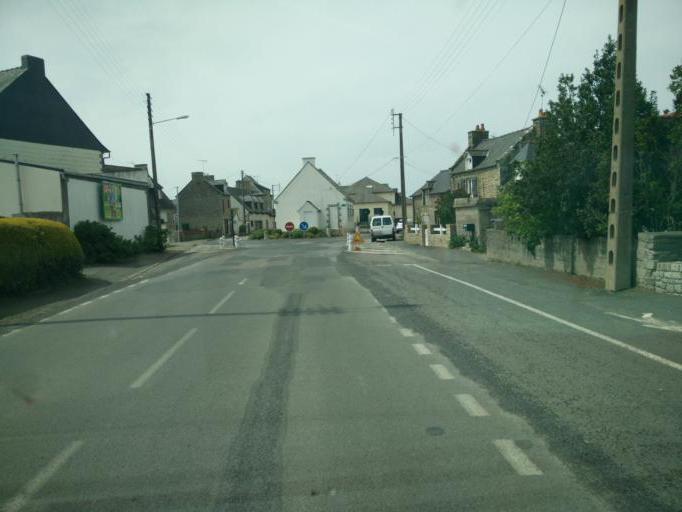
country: FR
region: Brittany
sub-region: Departement des Cotes-d'Armor
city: Matignon
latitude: 48.5944
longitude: -2.2856
